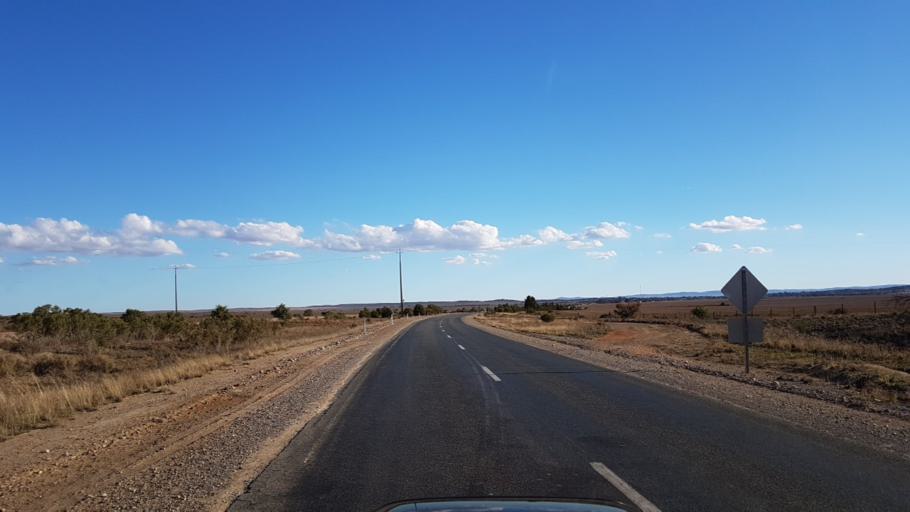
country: AU
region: South Australia
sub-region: Peterborough
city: Peterborough
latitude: -32.9597
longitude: 138.8918
